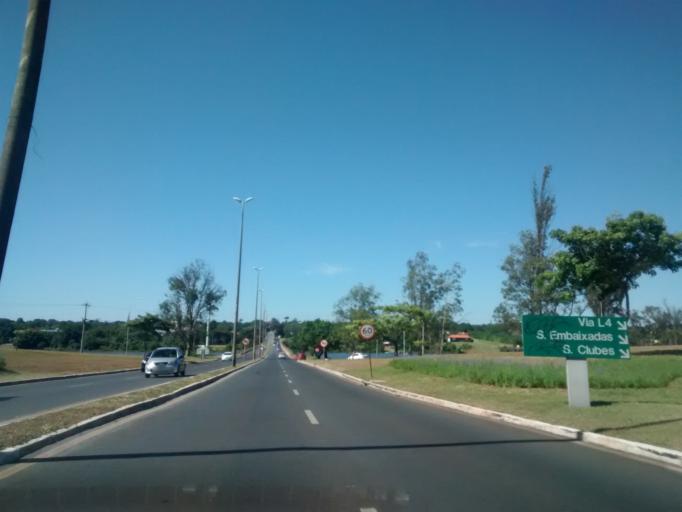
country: BR
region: Federal District
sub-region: Brasilia
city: Brasilia
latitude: -15.8364
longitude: -47.8995
